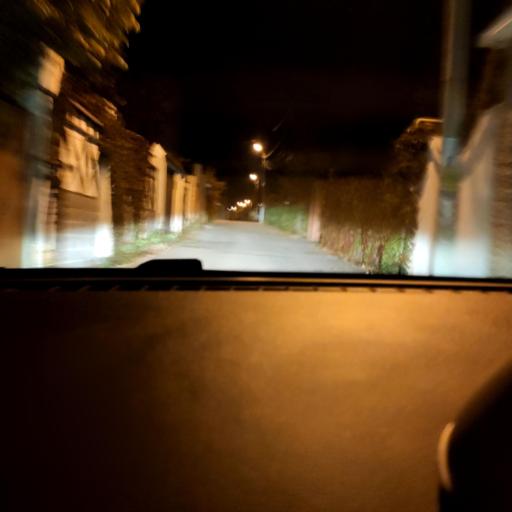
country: RU
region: Samara
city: Samara
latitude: 53.2521
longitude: 50.1925
